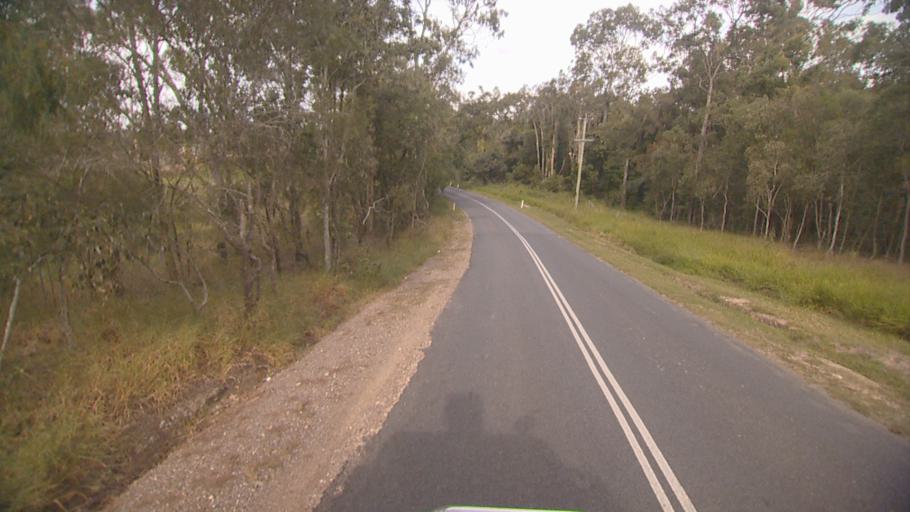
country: AU
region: Queensland
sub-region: Logan
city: Beenleigh
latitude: -27.7140
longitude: 153.1705
